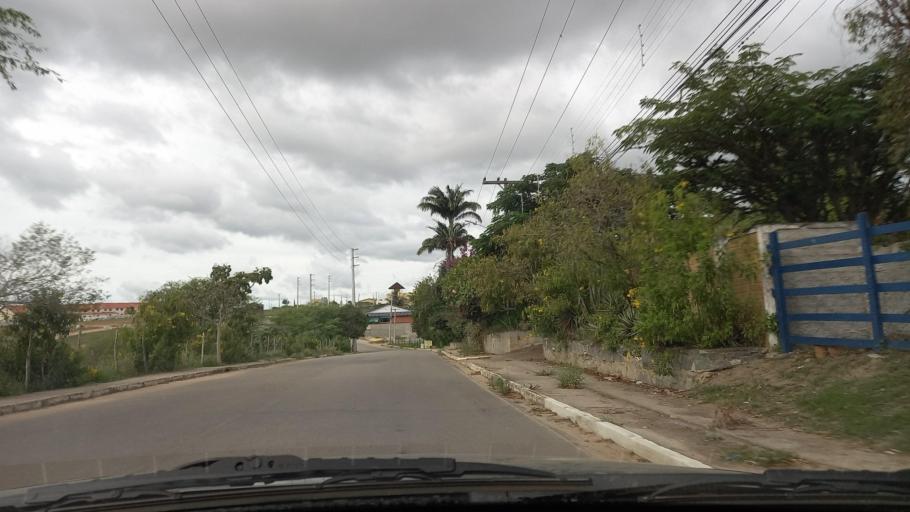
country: BR
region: Pernambuco
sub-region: Gravata
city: Gravata
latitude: -8.2039
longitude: -35.5527
